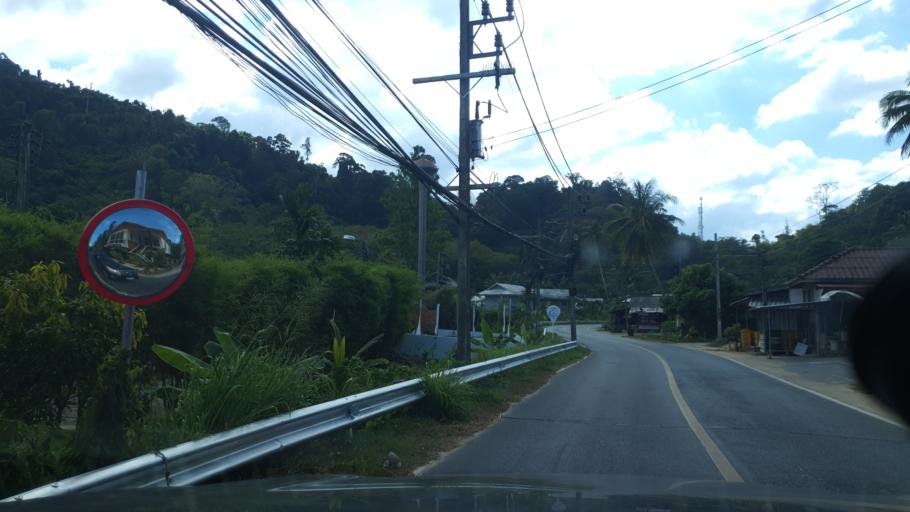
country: TH
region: Phuket
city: Thalang
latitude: 8.0665
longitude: 98.2921
